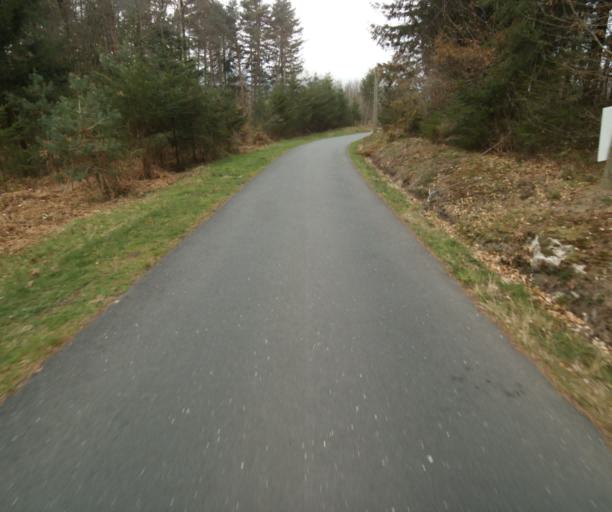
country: FR
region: Limousin
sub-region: Departement de la Correze
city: Correze
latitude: 45.2990
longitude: 1.9161
